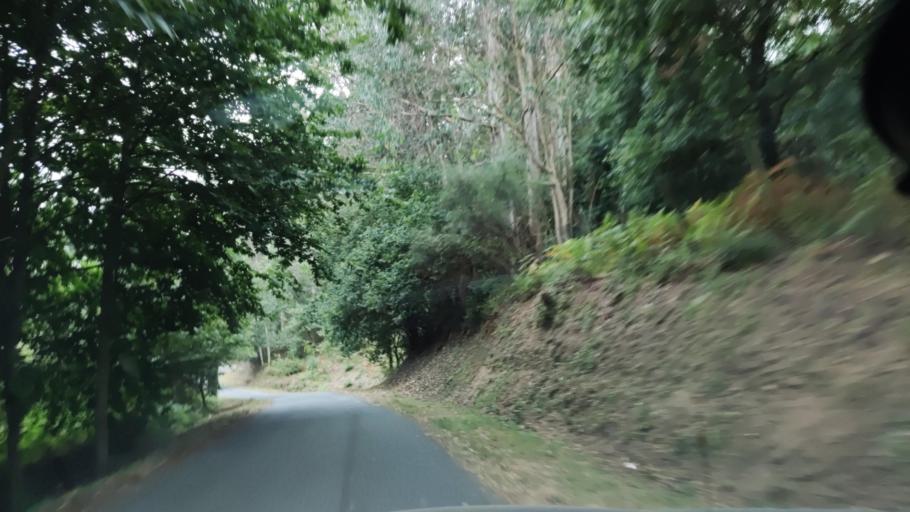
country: ES
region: Galicia
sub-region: Provincia de Pontevedra
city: Catoira
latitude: 42.7003
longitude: -8.7267
